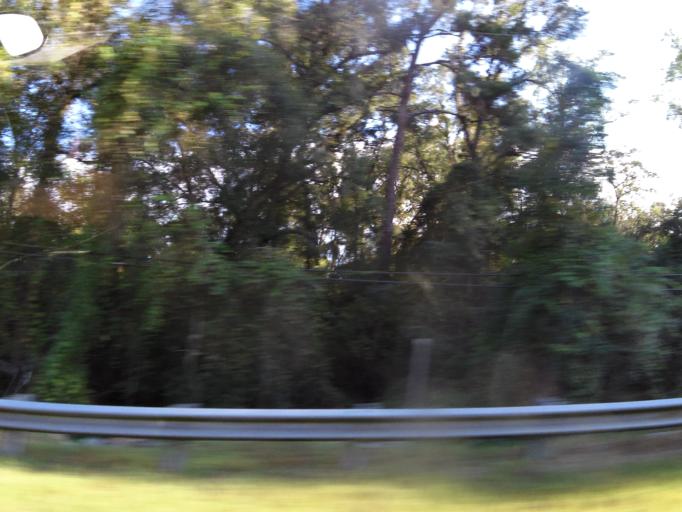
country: US
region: Georgia
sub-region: Brooks County
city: Quitman
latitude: 30.7880
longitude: -83.5072
